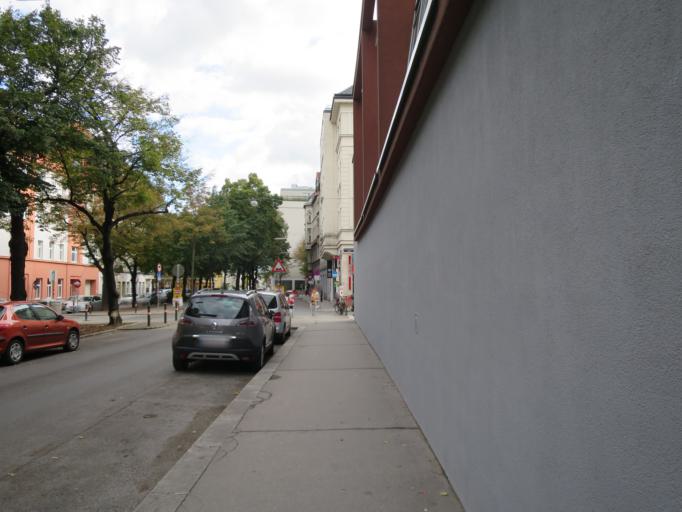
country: AT
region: Vienna
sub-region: Wien Stadt
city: Vienna
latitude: 48.2011
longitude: 16.3299
